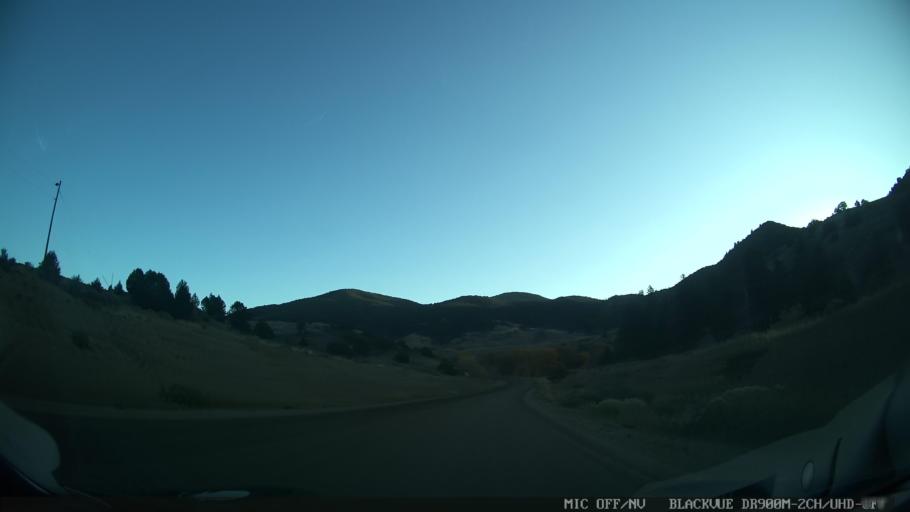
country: US
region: Colorado
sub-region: Grand County
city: Kremmling
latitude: 39.9275
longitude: -106.5299
